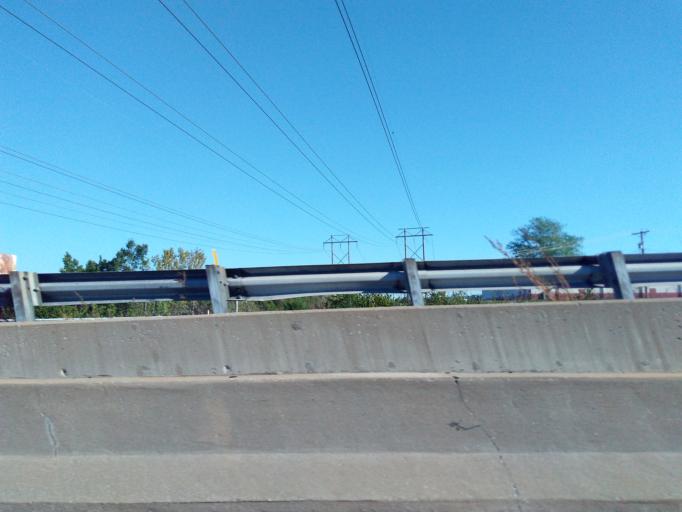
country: US
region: Missouri
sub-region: Saint Louis County
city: Green Park
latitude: 38.5049
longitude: -90.3430
